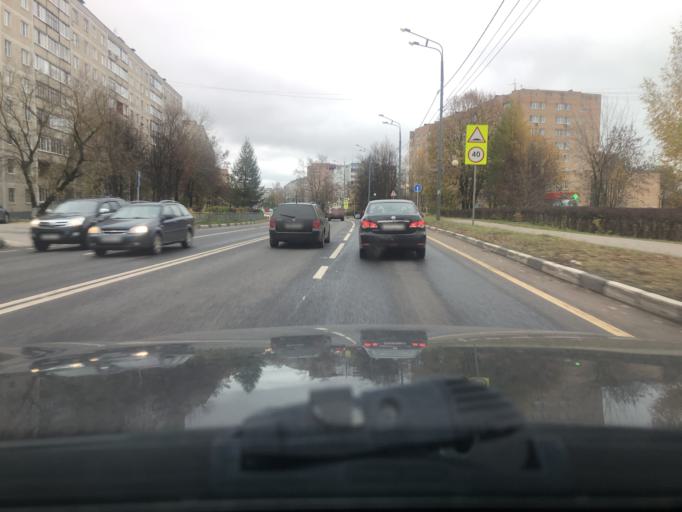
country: RU
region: Moskovskaya
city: Sergiyev Posad
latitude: 56.3283
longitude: 38.1320
